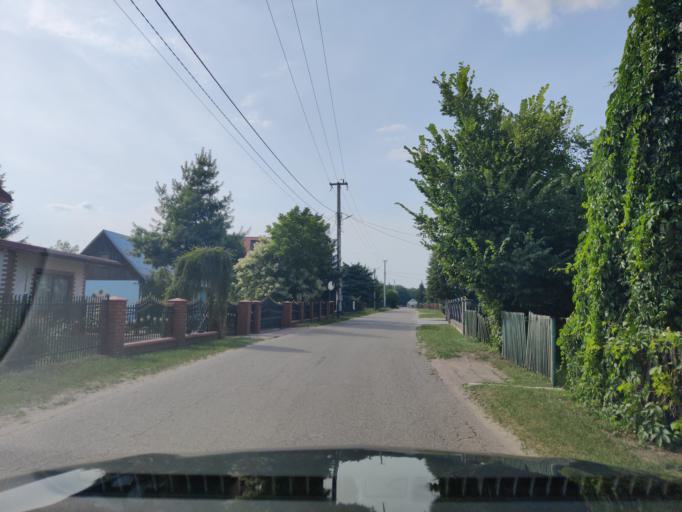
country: PL
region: Masovian Voivodeship
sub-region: Powiat wyszkowski
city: Rzasnik
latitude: 52.7399
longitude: 21.3338
